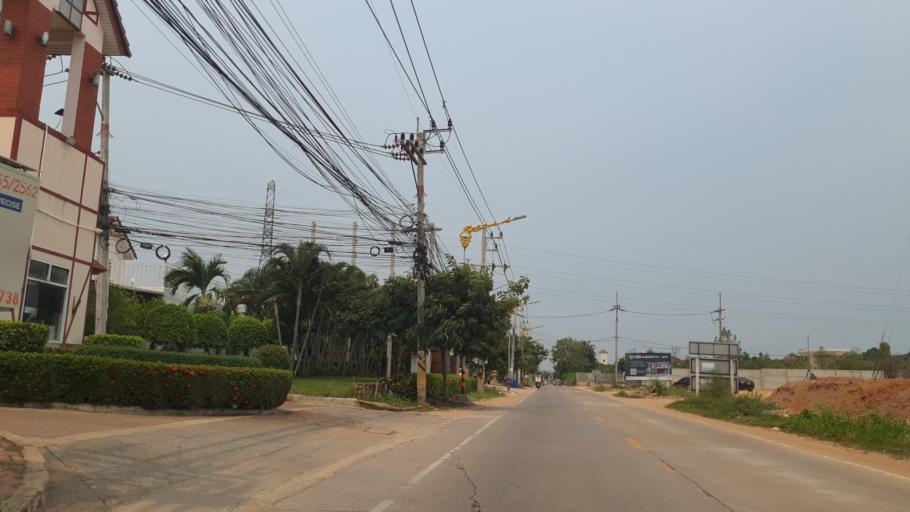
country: TH
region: Chon Buri
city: Phatthaya
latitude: 12.8959
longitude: 100.9202
